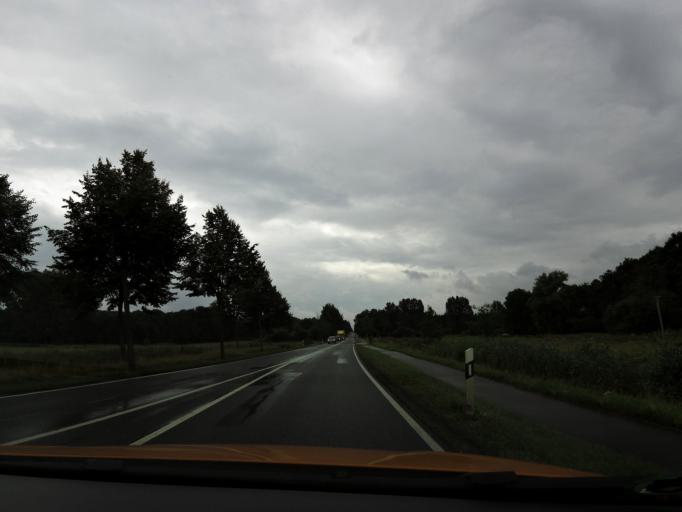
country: DE
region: Lower Saxony
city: Bassum
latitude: 52.8348
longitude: 8.7353
